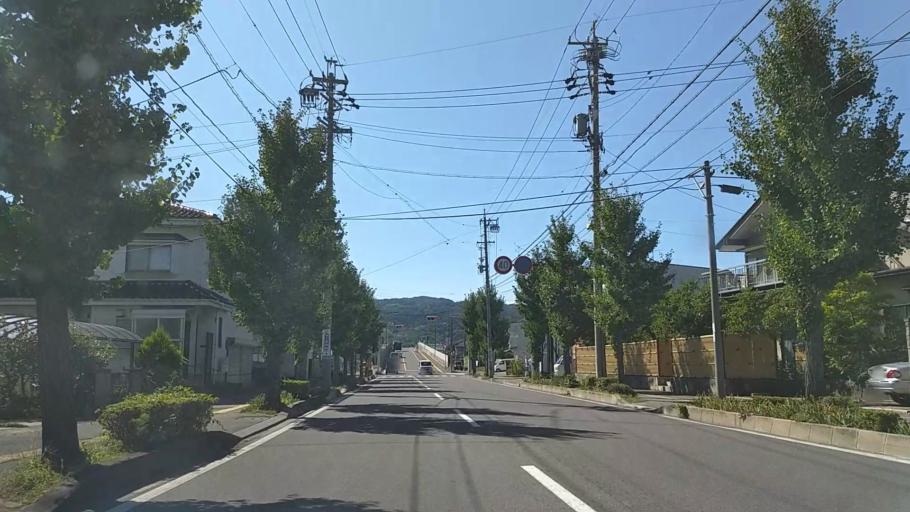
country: JP
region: Nagano
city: Nagano-shi
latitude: 36.5825
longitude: 138.1434
